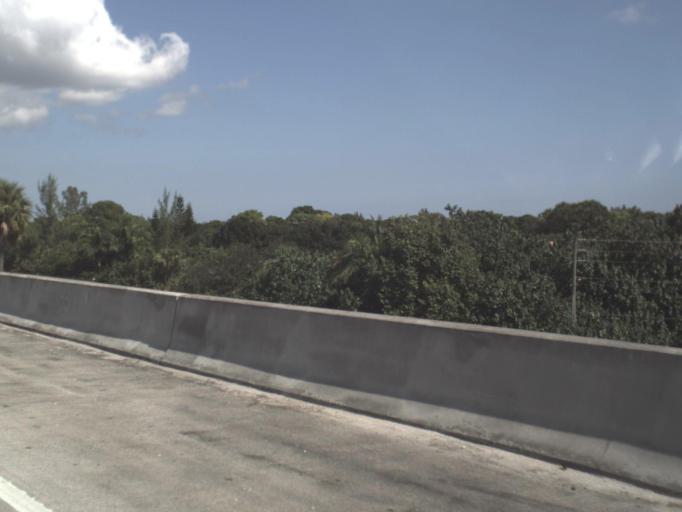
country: US
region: Florida
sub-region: Palm Beach County
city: Palm Beach Gardens
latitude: 26.7957
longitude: -80.1316
